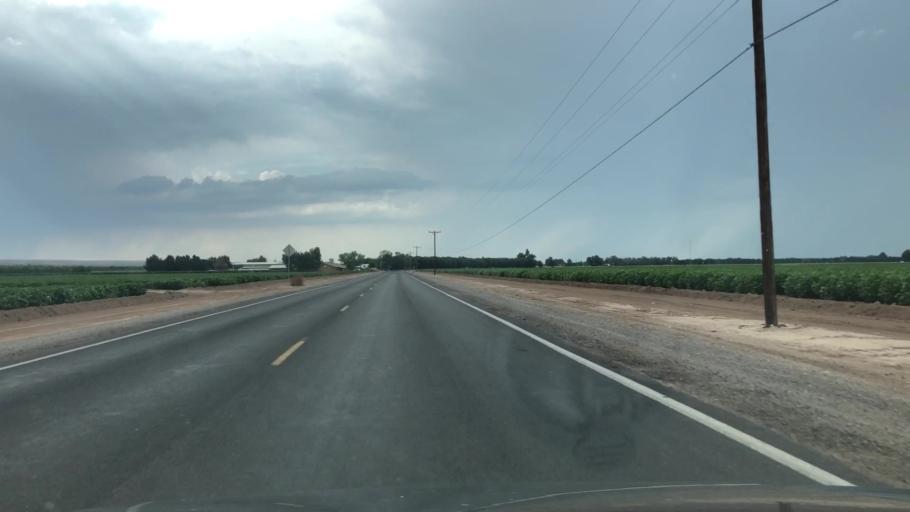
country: US
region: New Mexico
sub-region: Dona Ana County
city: La Union
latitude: 31.9650
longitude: -106.6486
